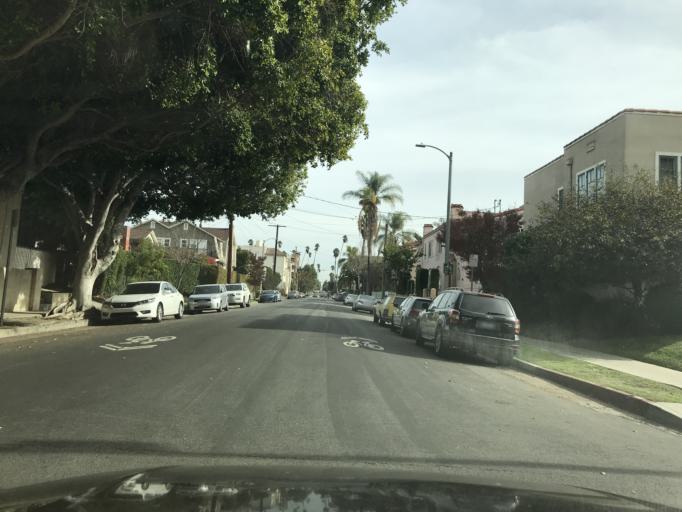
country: US
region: California
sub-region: Los Angeles County
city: Hollywood
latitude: 34.0671
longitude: -118.3163
